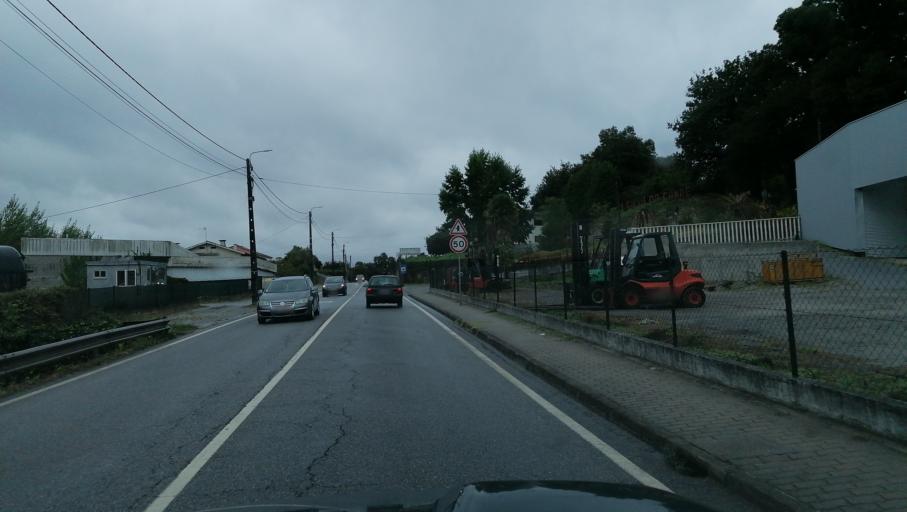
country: PT
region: Braga
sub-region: Guimaraes
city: Moreira de Conegos
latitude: 41.3900
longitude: -8.3350
